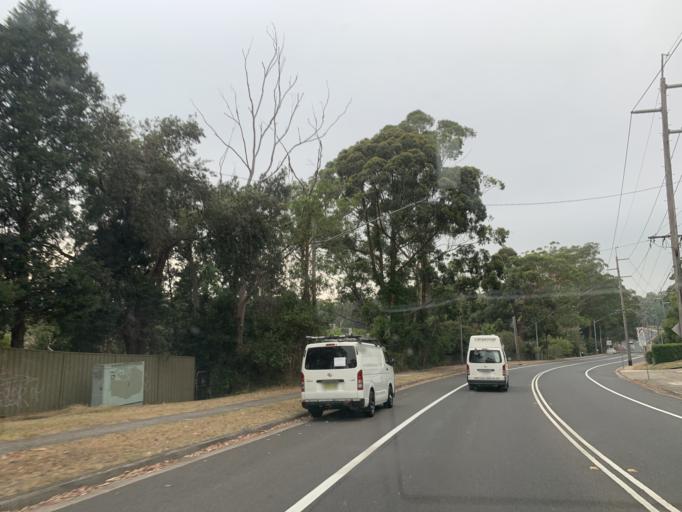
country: AU
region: New South Wales
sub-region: The Hills Shire
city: West Pennant
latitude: -33.7313
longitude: 151.0434
